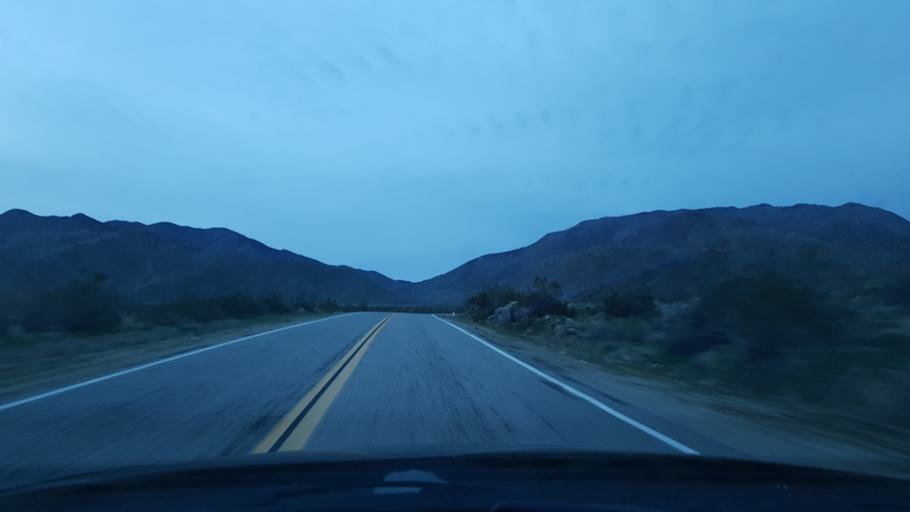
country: US
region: California
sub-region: San Diego County
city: Julian
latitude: 32.9999
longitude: -116.4505
